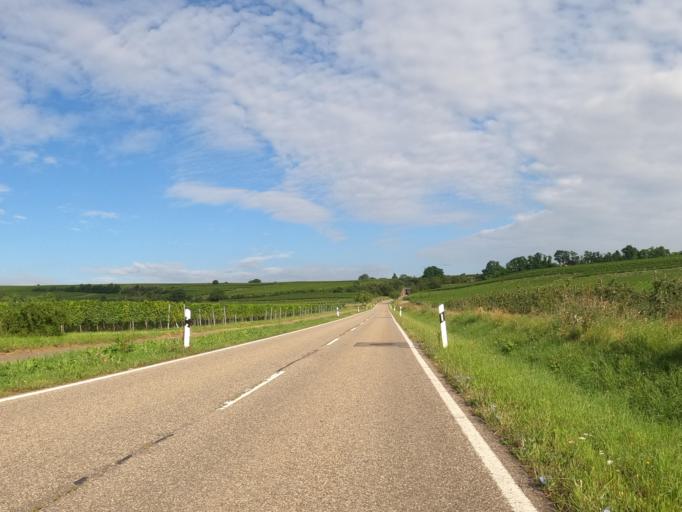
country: DE
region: Rheinland-Pfalz
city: Dackenheim
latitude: 49.5157
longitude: 8.1962
